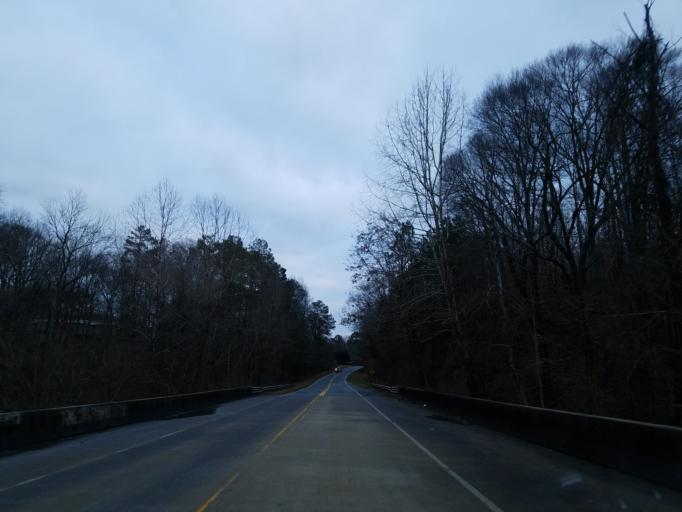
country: US
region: Georgia
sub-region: Bartow County
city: Emerson
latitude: 34.1012
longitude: -84.7374
